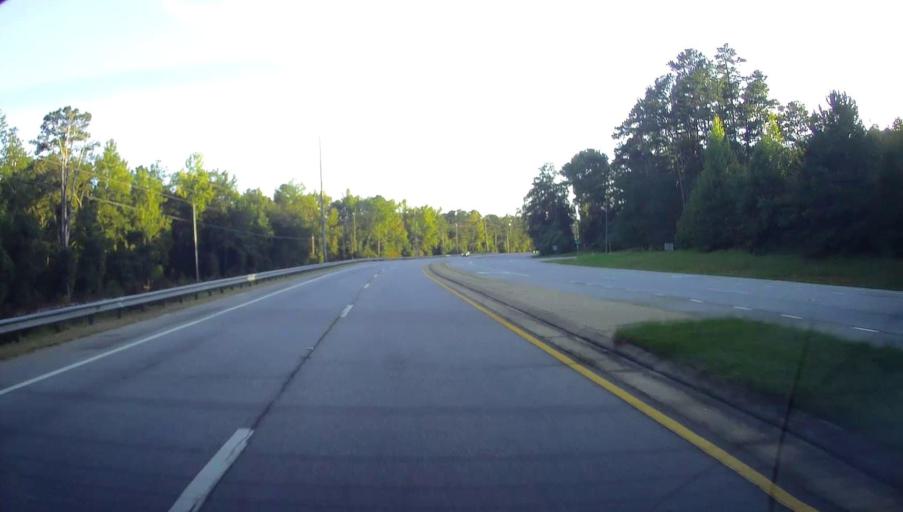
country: US
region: Georgia
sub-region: Muscogee County
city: Columbus
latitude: 32.5296
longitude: -84.8538
